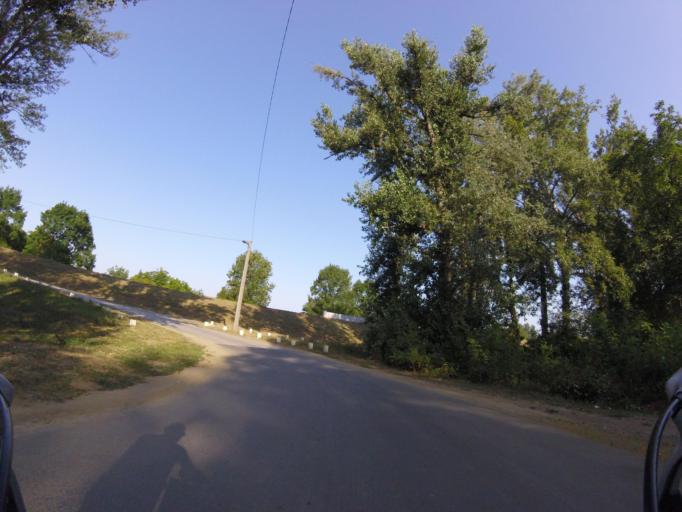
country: HU
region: Szabolcs-Szatmar-Bereg
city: Tarpa
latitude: 48.0641
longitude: 22.5182
